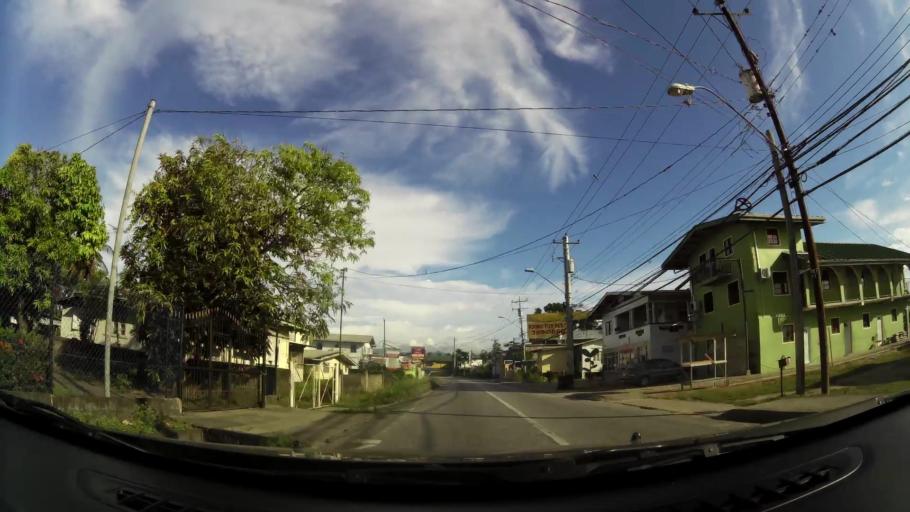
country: TT
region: Tunapuna/Piarco
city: Tunapuna
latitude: 10.5693
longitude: -61.3733
